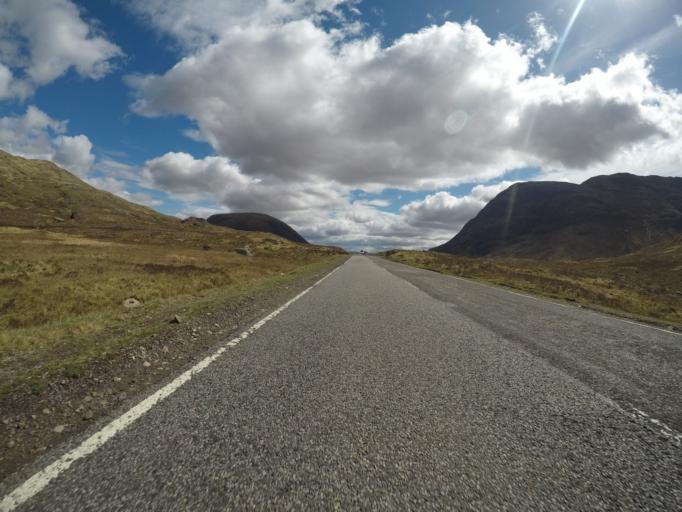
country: GB
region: Scotland
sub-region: Highland
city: Spean Bridge
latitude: 56.6632
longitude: -4.9330
